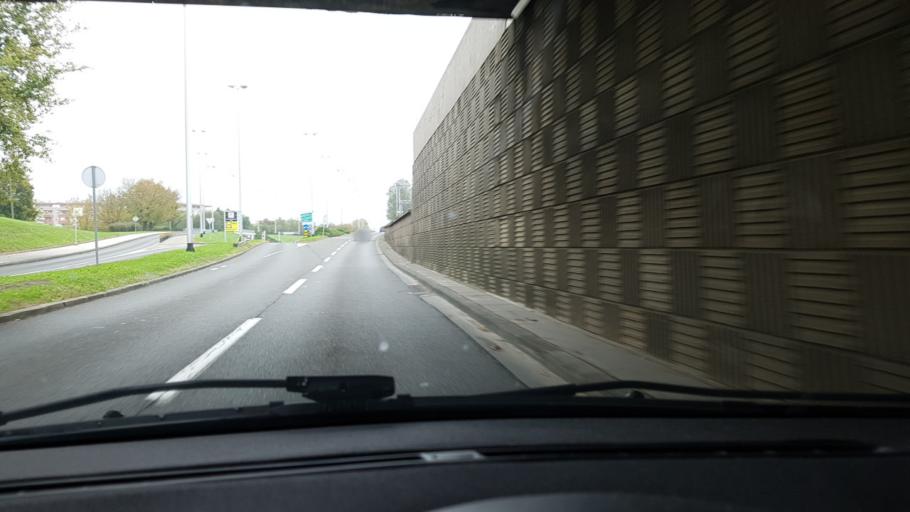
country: HR
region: Grad Zagreb
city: Stenjevec
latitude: 45.8145
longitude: 15.8608
